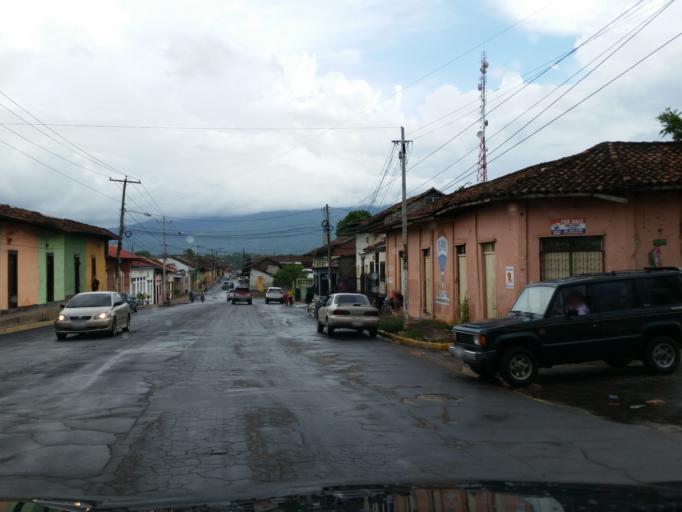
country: NI
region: Granada
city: Granada
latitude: 11.9309
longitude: -85.9623
